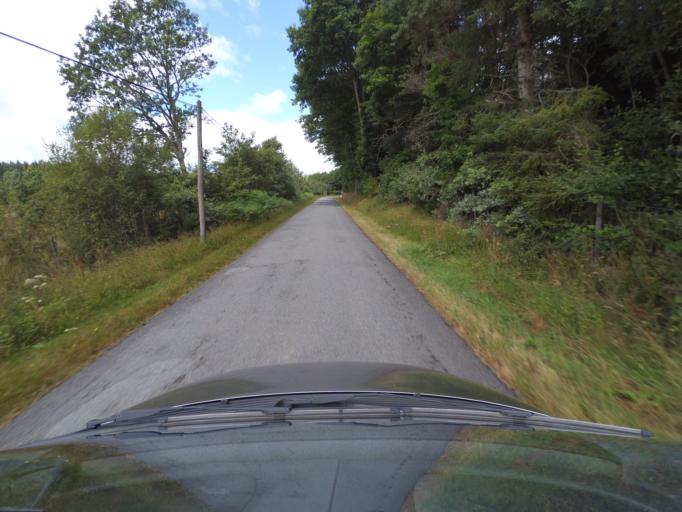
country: FR
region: Limousin
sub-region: Departement de la Creuse
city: Banize
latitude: 45.7712
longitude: 1.9442
